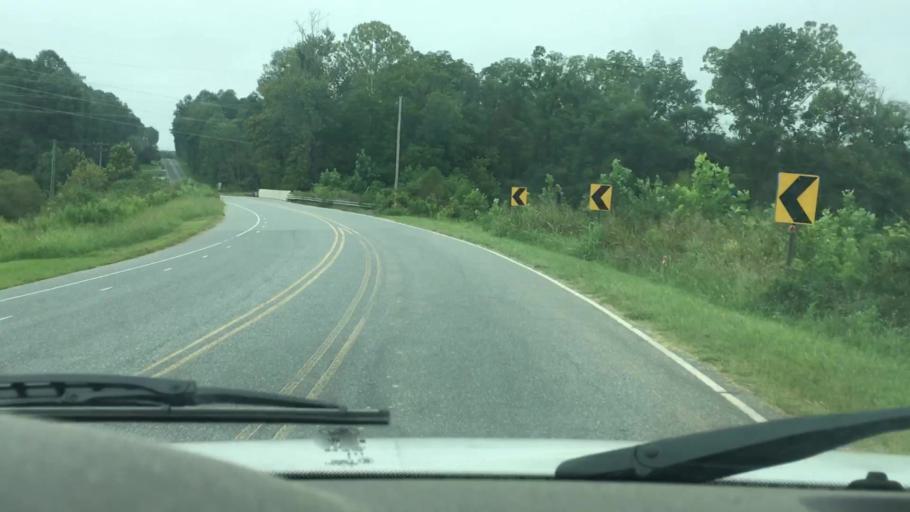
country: US
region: North Carolina
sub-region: Gaston County
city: Davidson
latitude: 35.5196
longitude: -80.8146
